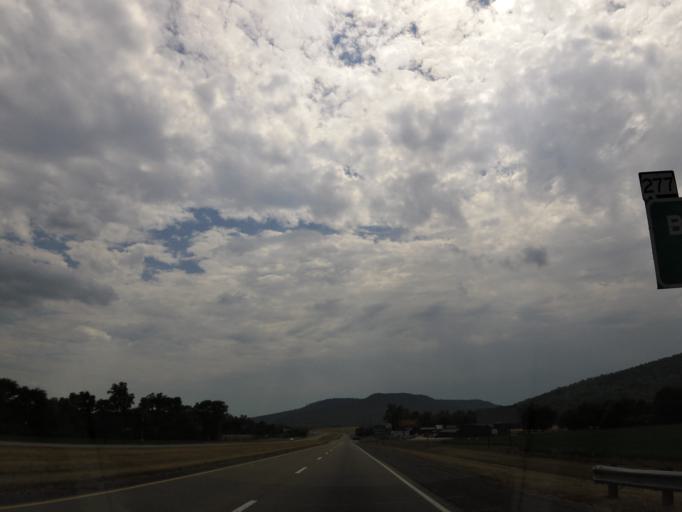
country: US
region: Tennessee
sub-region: Marion County
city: South Pittsburg
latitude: 34.9840
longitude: -85.7249
